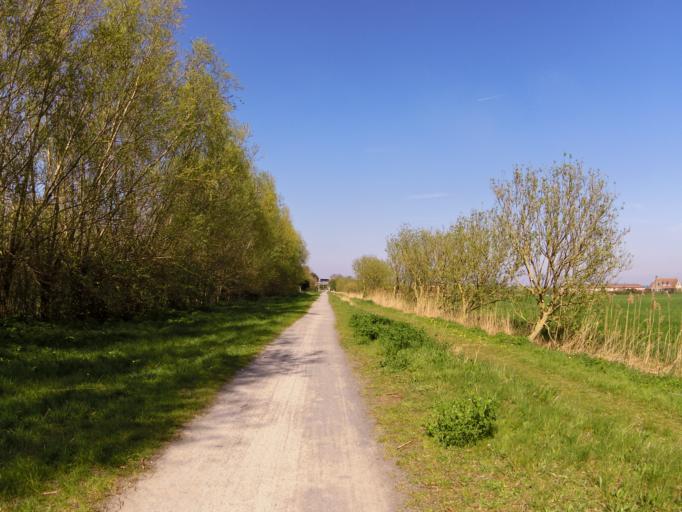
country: BE
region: Flanders
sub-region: Provincie West-Vlaanderen
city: Nieuwpoort
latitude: 51.1127
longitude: 2.7659
